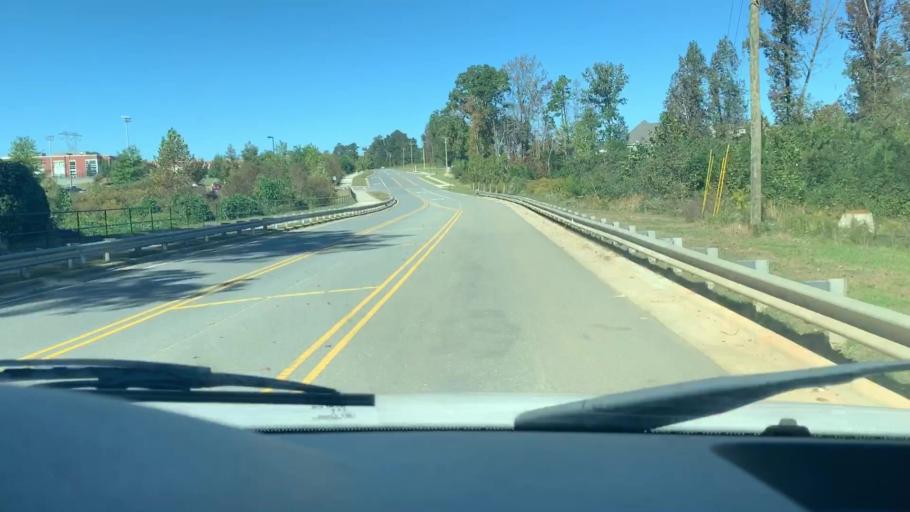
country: US
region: North Carolina
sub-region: Gaston County
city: Davidson
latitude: 35.4670
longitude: -80.8239
